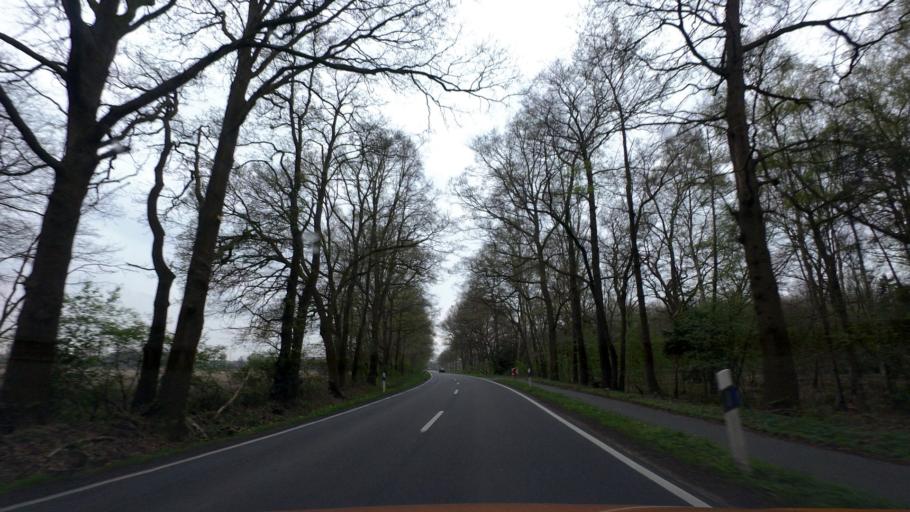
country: DE
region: Lower Saxony
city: Dinklage
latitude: 52.6917
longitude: 8.1579
